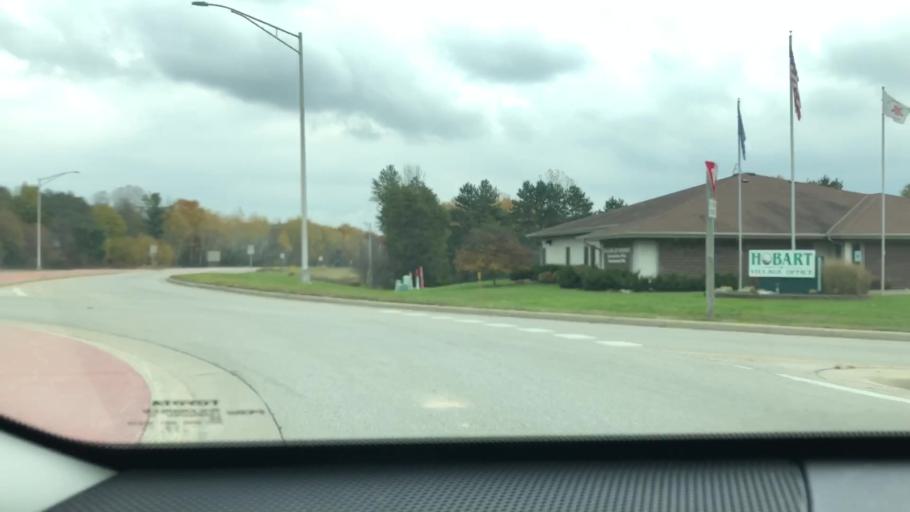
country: US
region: Wisconsin
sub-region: Brown County
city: Oneida
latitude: 44.4994
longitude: -88.1498
